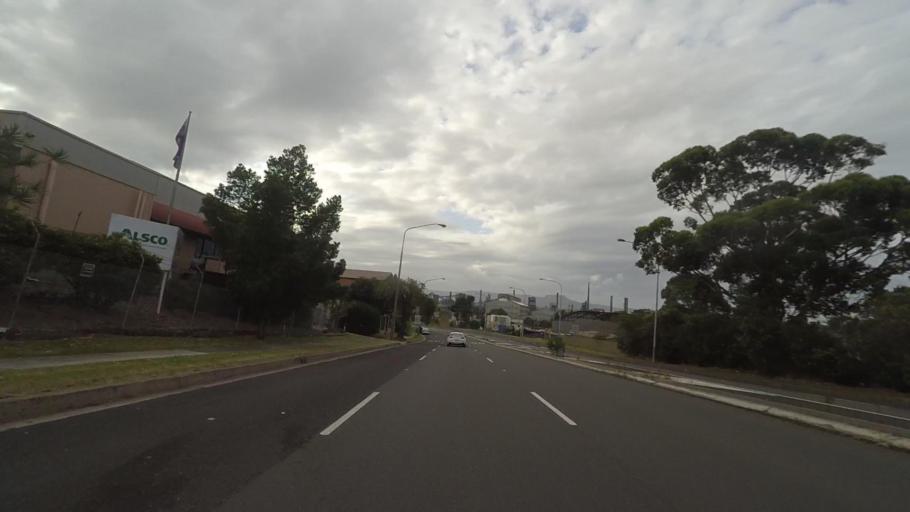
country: AU
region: New South Wales
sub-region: Wollongong
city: Port Kembla
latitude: -34.4791
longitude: 150.9012
